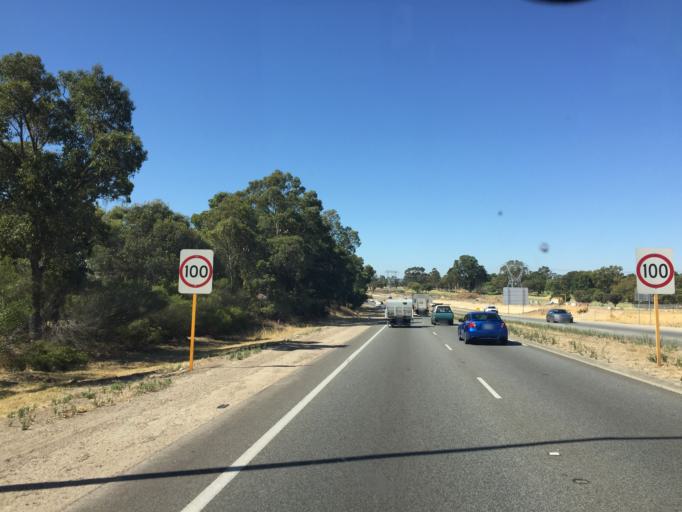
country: AU
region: Western Australia
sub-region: Kalamunda
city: Maida Vale
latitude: -31.9394
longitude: 116.0166
